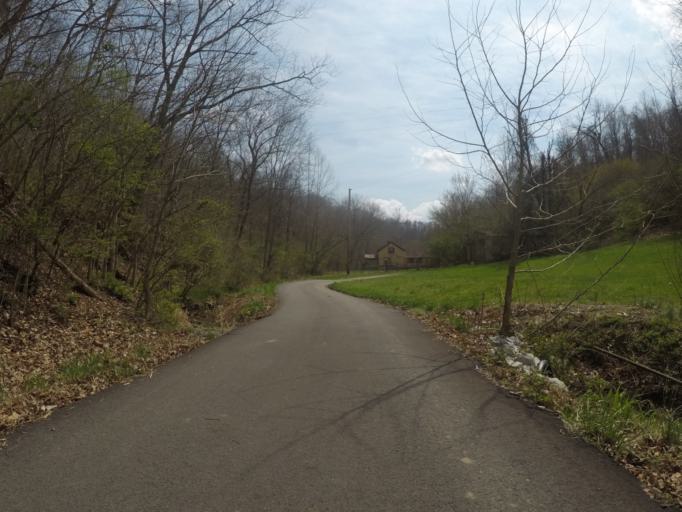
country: US
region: West Virginia
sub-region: Cabell County
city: Pea Ridge
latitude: 38.3913
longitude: -82.3481
